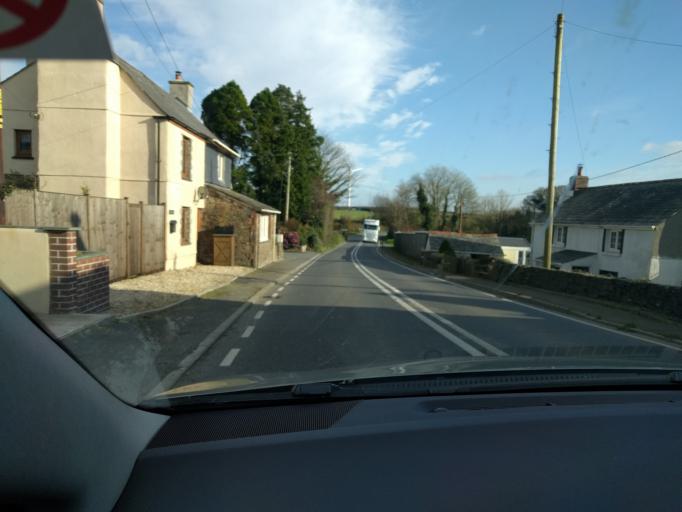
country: GB
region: England
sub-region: Cornwall
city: Trewen
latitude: 50.6311
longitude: -4.4622
